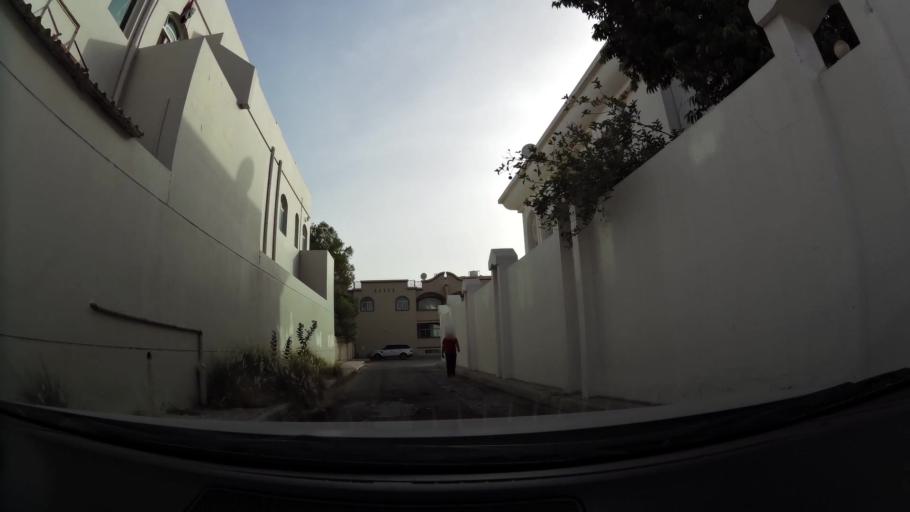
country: AE
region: Abu Dhabi
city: Al Ain
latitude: 24.2209
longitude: 55.7130
